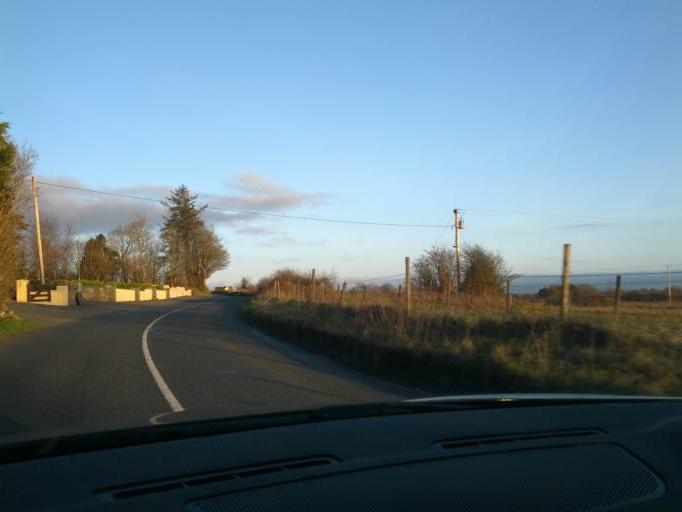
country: IE
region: Connaught
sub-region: Sligo
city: Tobercurry
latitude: 54.0503
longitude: -8.6989
